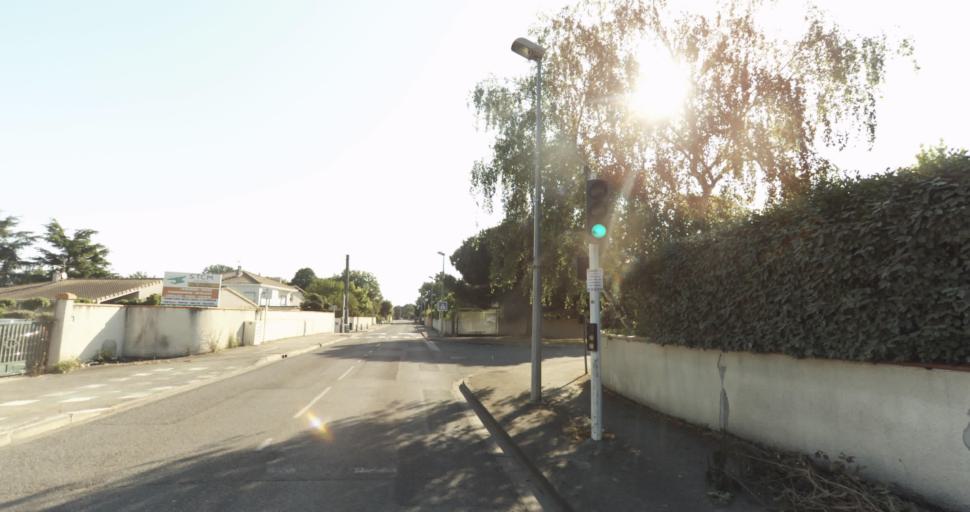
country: FR
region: Midi-Pyrenees
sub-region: Departement de la Haute-Garonne
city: La Salvetat-Saint-Gilles
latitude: 43.5742
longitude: 1.2535
